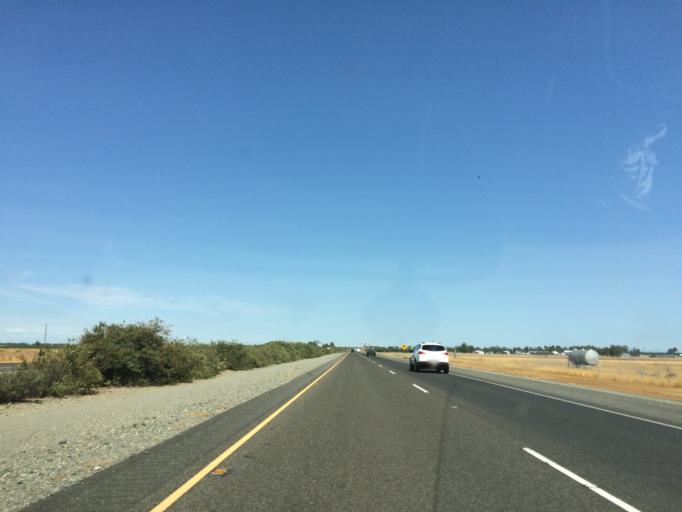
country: US
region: California
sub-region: Glenn County
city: Orland
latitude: 39.6864
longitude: -122.2047
